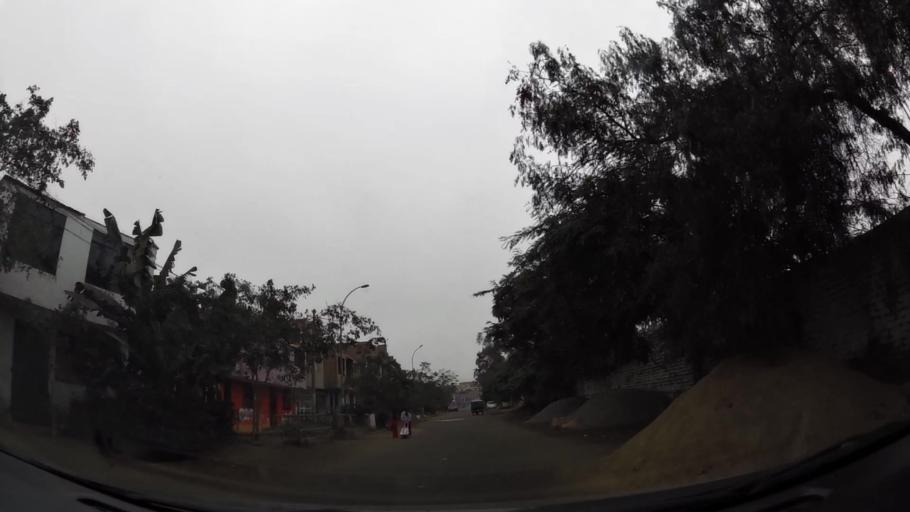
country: PE
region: Lima
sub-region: Lima
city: Urb. Santo Domingo
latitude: -11.8729
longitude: -77.0737
